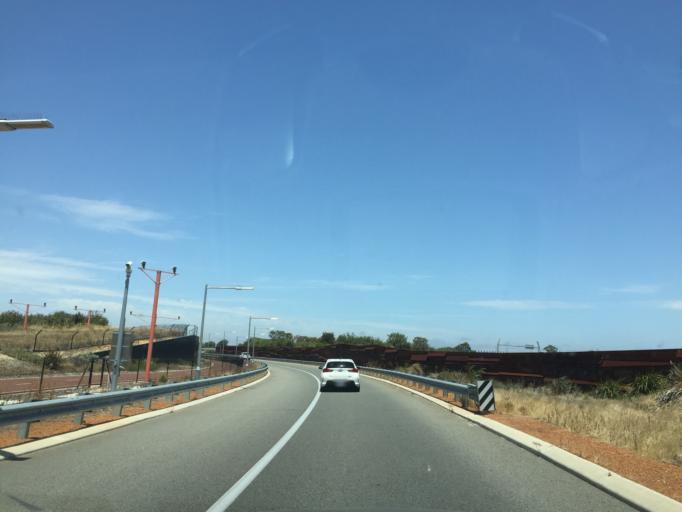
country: AU
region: Western Australia
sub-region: Belmont
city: Kewdale
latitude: -31.9637
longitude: 115.9583
